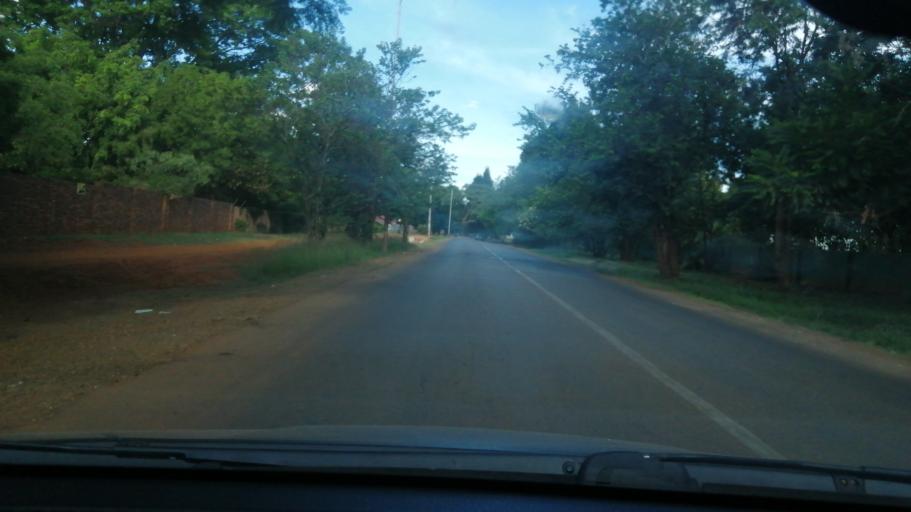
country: ZW
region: Harare
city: Harare
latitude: -17.7619
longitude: 31.0805
